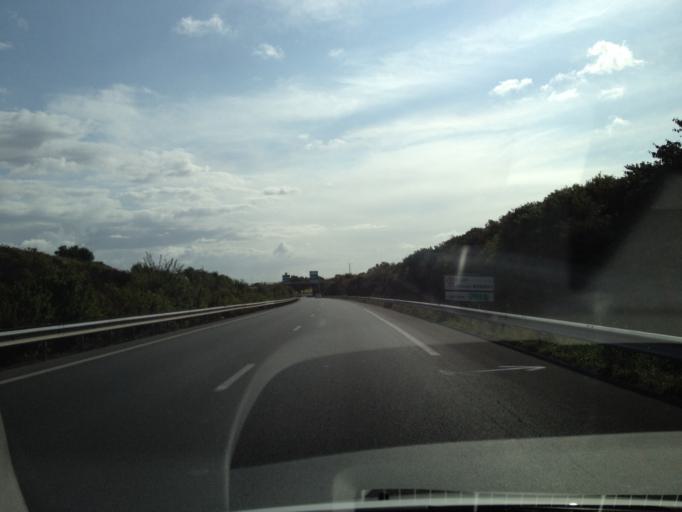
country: FR
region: Poitou-Charentes
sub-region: Departement de la Charente-Maritime
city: Sainte-Soulle
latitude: 46.1997
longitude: -1.0341
